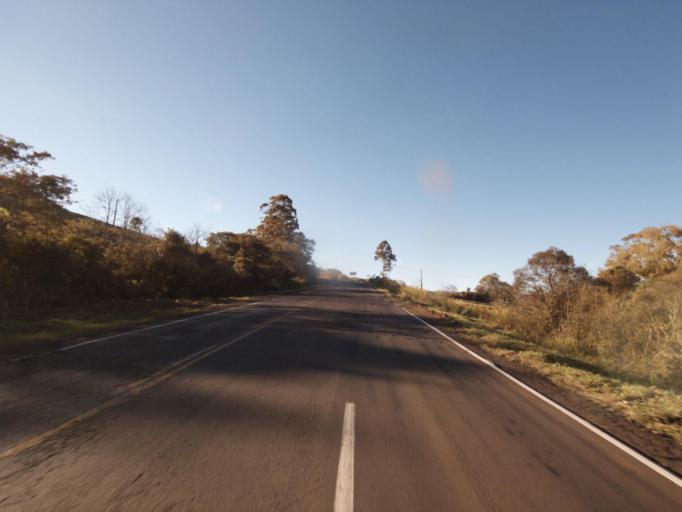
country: AR
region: Misiones
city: Bernardo de Irigoyen
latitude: -26.3315
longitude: -53.5447
